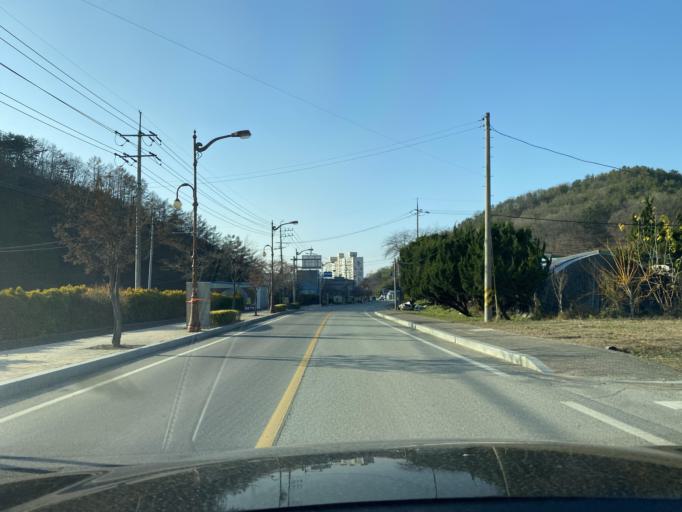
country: KR
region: Chungcheongnam-do
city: Yesan
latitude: 36.6797
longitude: 126.8604
